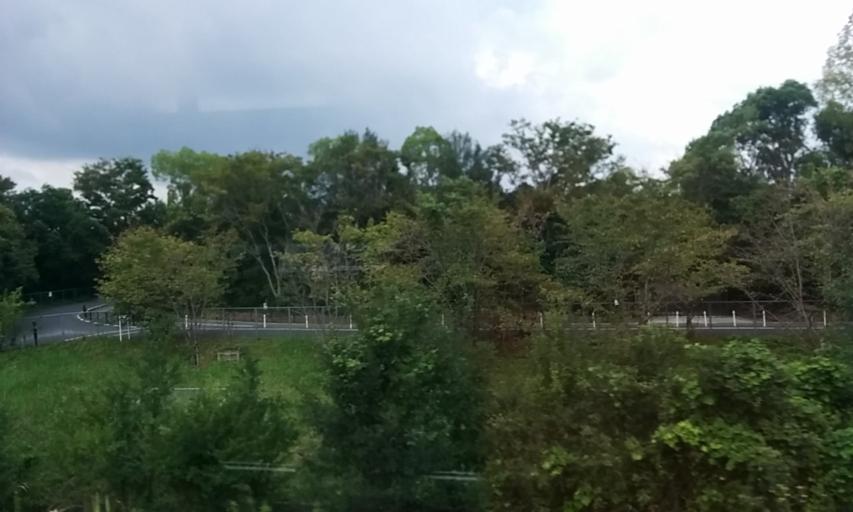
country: JP
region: Nara
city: Tawaramoto
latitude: 34.5940
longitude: 135.7848
